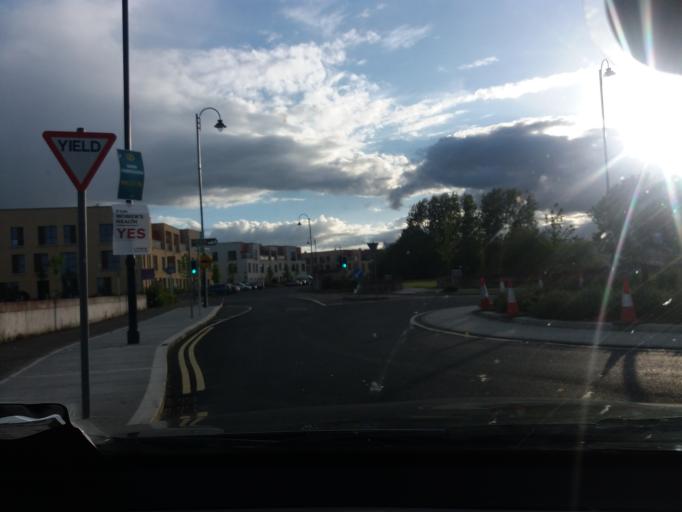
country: IE
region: Leinster
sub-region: South Dublin
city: Newcastle
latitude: 53.2956
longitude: -6.4913
